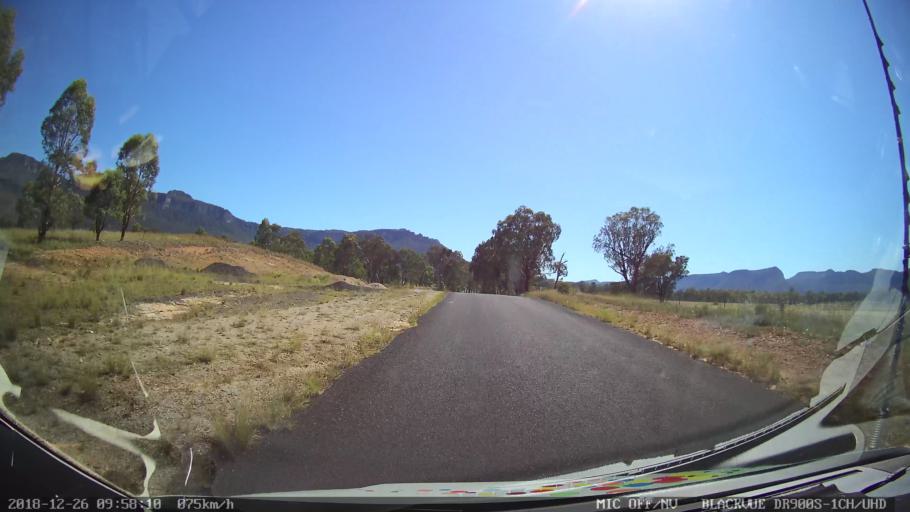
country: AU
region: New South Wales
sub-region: Mid-Western Regional
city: Kandos
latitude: -33.0392
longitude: 150.2019
